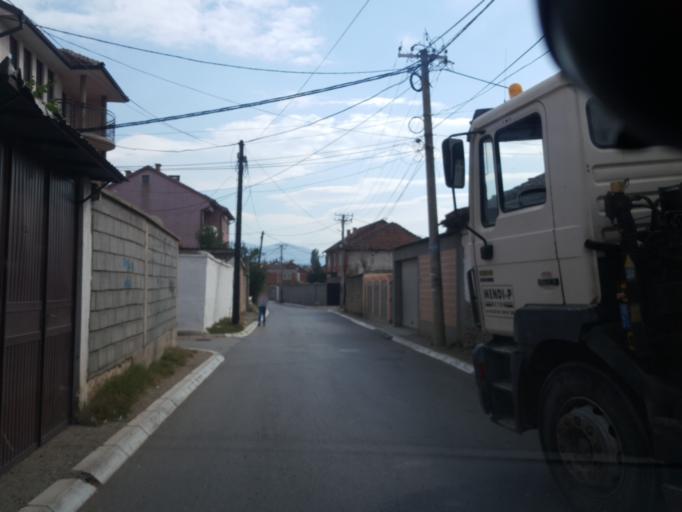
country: XK
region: Gjakova
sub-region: Komuna e Gjakoves
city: Gjakove
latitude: 42.3735
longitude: 20.4295
